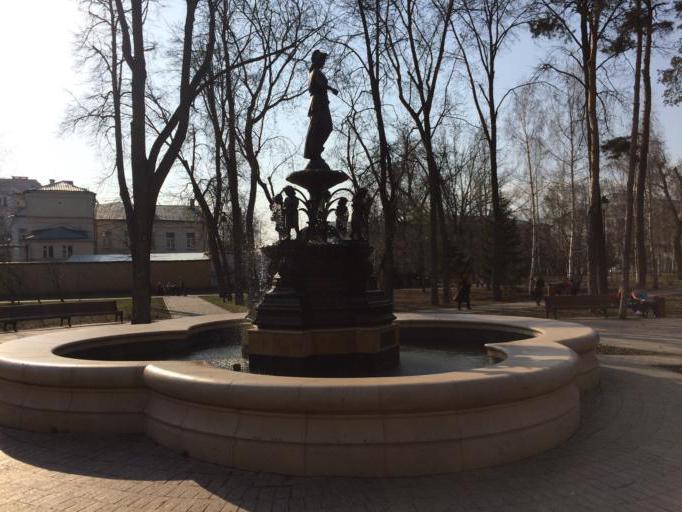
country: RU
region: Tatarstan
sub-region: Gorod Kazan'
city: Kazan
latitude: 55.7928
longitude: 49.1340
